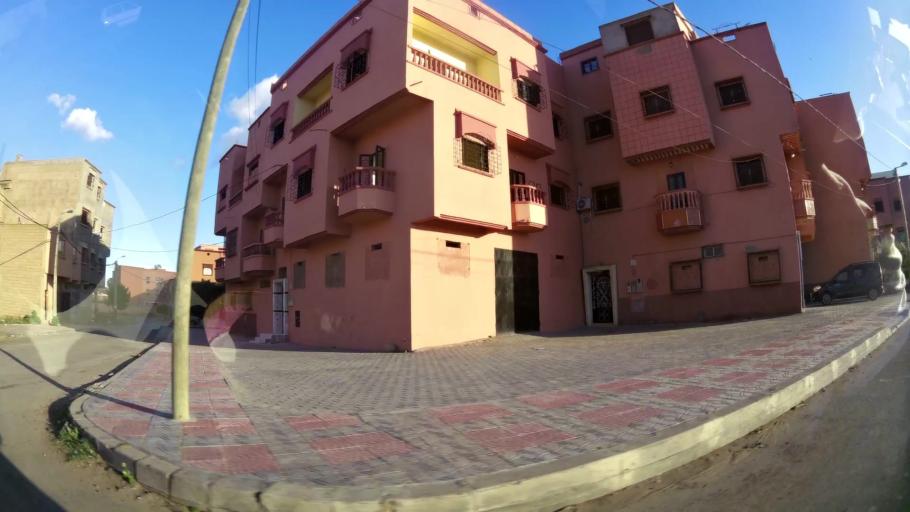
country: MA
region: Marrakech-Tensift-Al Haouz
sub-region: Kelaa-Des-Sraghna
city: Sidi Abdallah
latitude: 32.2419
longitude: -7.9610
